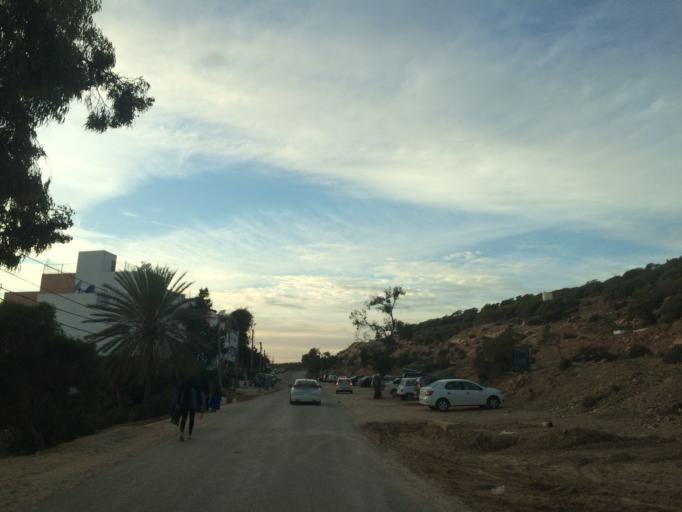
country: MA
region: Souss-Massa-Draa
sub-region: Agadir-Ida-ou-Tnan
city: Taghazout
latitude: 30.5456
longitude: -9.7120
